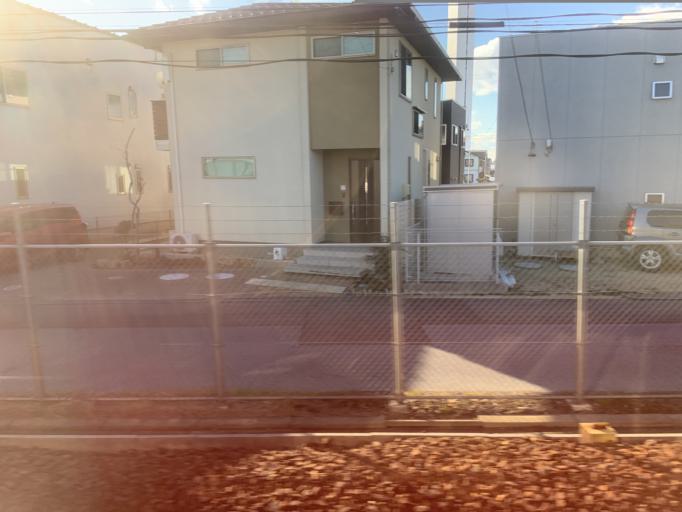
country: JP
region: Aichi
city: Inazawa
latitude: 35.2459
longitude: 136.8244
